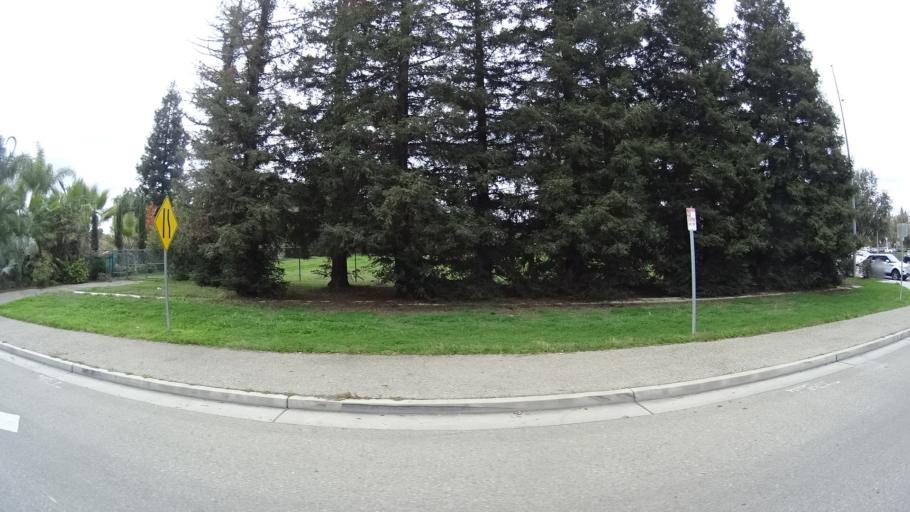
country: US
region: California
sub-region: Fresno County
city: Fresno
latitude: 36.8369
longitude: -119.8355
